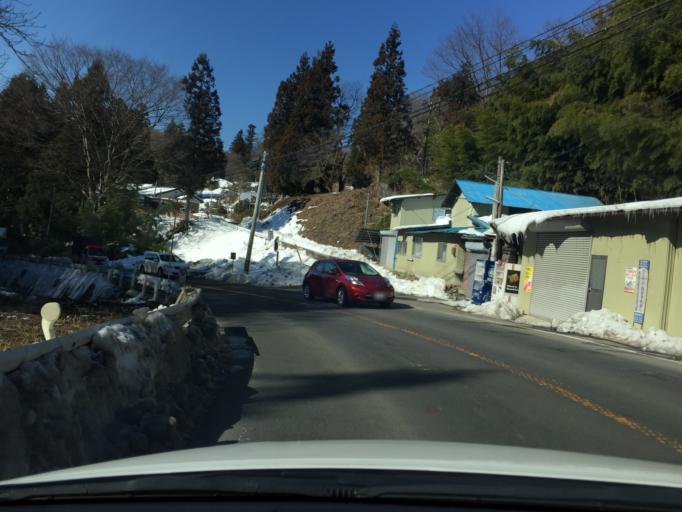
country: JP
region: Fukushima
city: Yanagawamachi-saiwaicho
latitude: 37.7568
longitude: 140.6797
